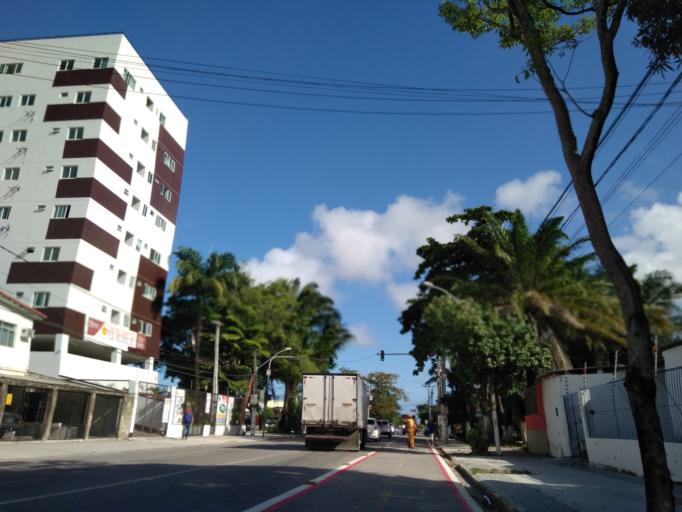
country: BR
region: Pernambuco
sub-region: Recife
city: Recife
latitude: -8.0886
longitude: -34.9102
